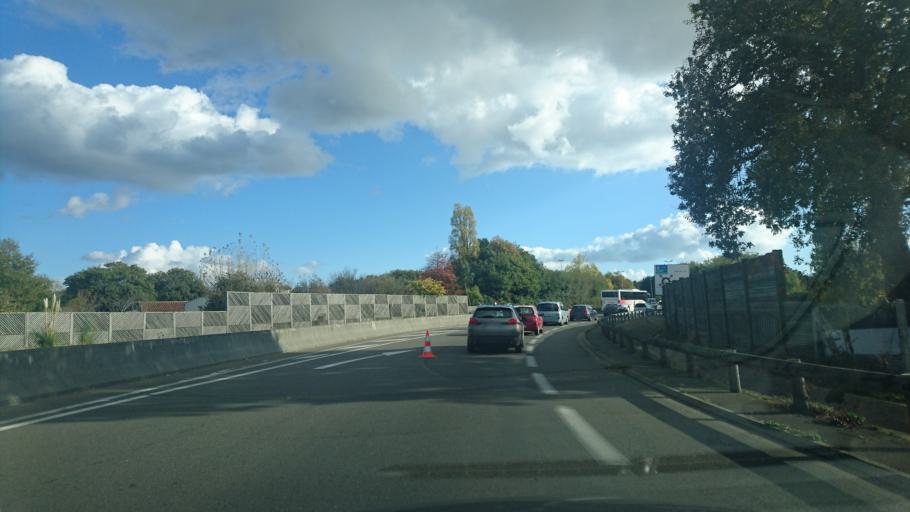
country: FR
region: Pays de la Loire
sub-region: Departement de la Vendee
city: Olonne-sur-Mer
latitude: 46.5167
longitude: -1.7605
